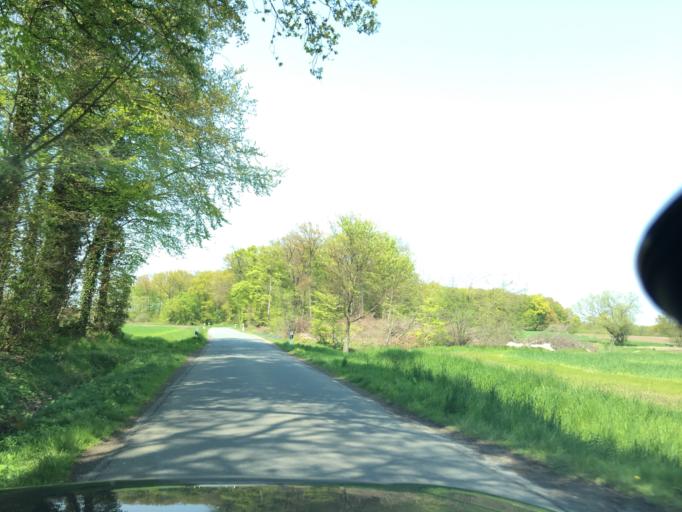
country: DE
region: North Rhine-Westphalia
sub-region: Regierungsbezirk Munster
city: Senden
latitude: 51.8149
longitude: 7.4707
